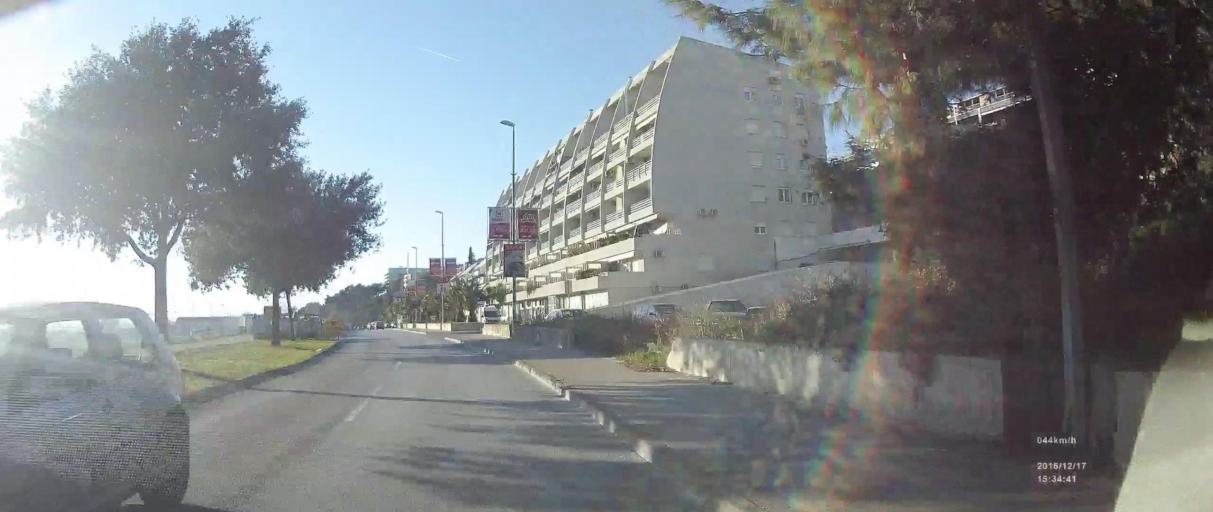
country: HR
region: Splitsko-Dalmatinska
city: Vranjic
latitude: 43.5036
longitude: 16.4782
